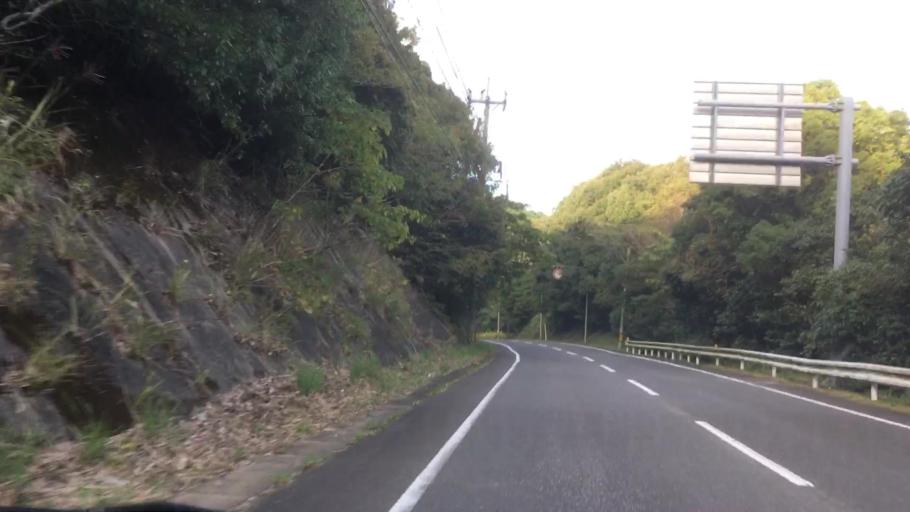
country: JP
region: Nagasaki
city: Sasebo
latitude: 32.9780
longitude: 129.7109
